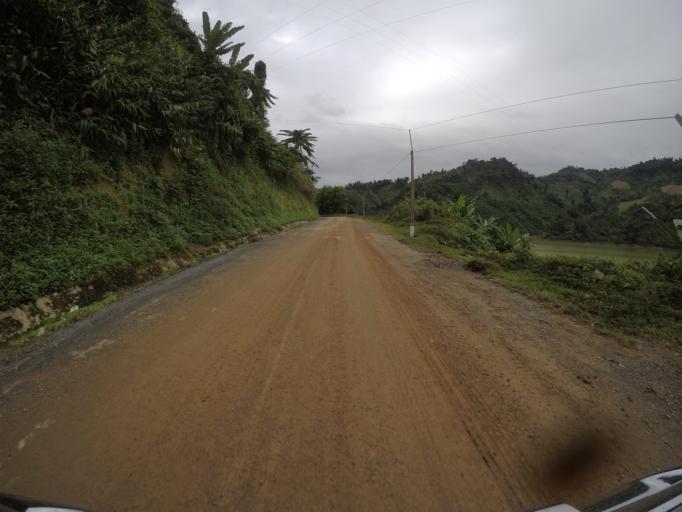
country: VN
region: Quang Nam
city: Thanh My
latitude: 15.6645
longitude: 107.6299
